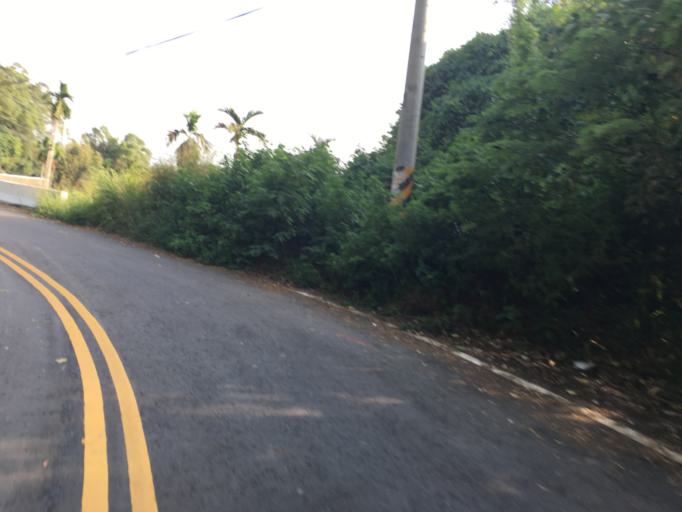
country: TW
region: Taiwan
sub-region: Hsinchu
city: Hsinchu
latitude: 24.7523
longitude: 121.0312
